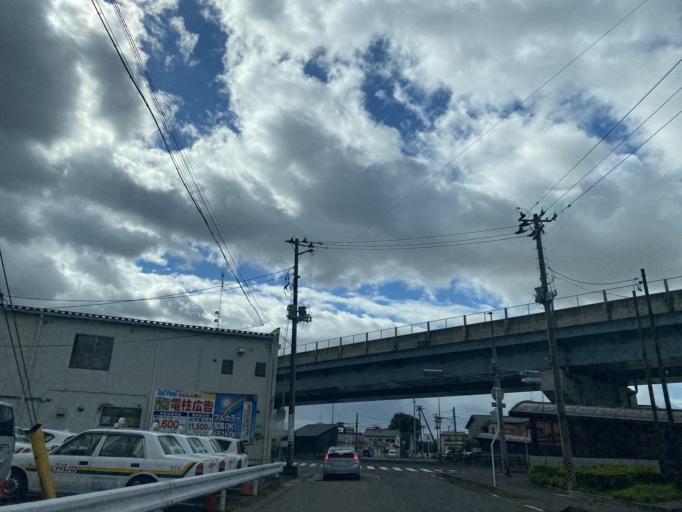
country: JP
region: Fukushima
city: Koriyama
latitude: 37.3887
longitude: 140.3425
